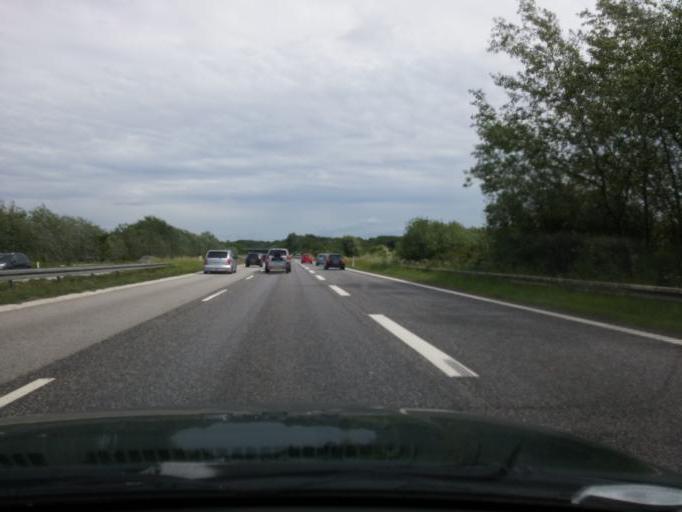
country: DK
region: South Denmark
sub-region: Assens Kommune
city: Tommerup Stationsby
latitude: 55.3907
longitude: 10.2009
